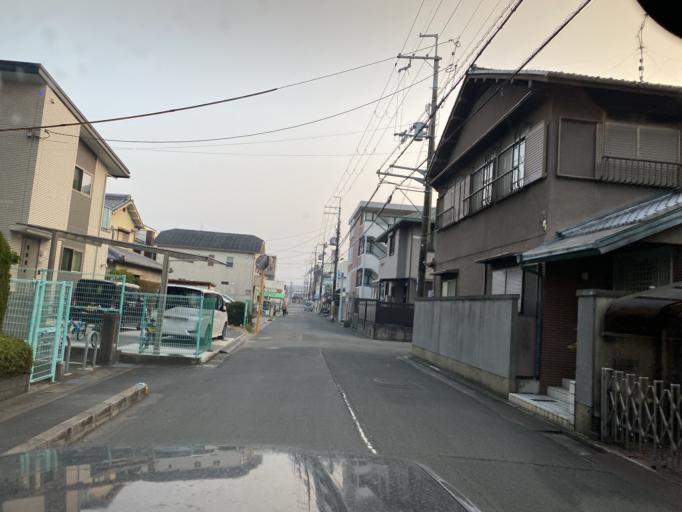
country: JP
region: Kyoto
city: Tanabe
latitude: 34.8220
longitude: 135.7750
